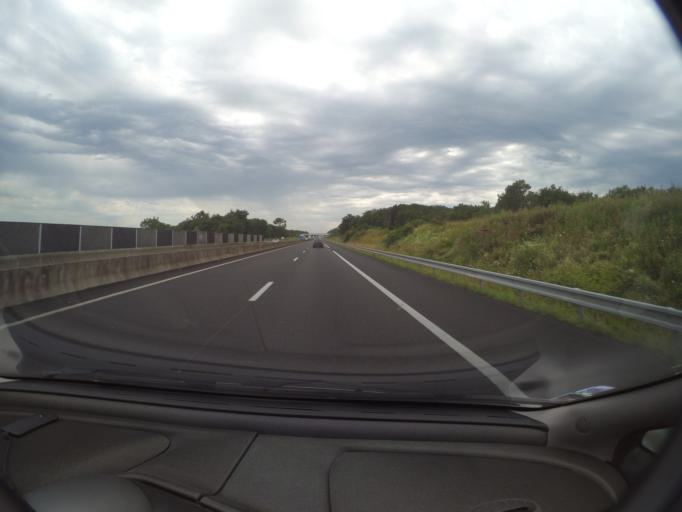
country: FR
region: Pays de la Loire
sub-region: Departement de Maine-et-Loire
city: Saint-Lambert-la-Potherie
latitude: 47.4769
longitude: -0.6730
